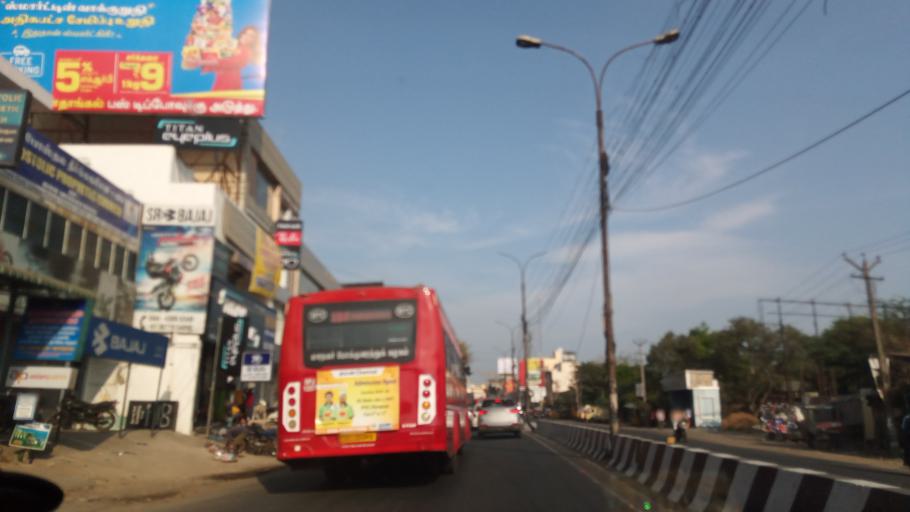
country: IN
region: Tamil Nadu
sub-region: Kancheepuram
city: Poonamalle
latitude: 13.0386
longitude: 80.1341
